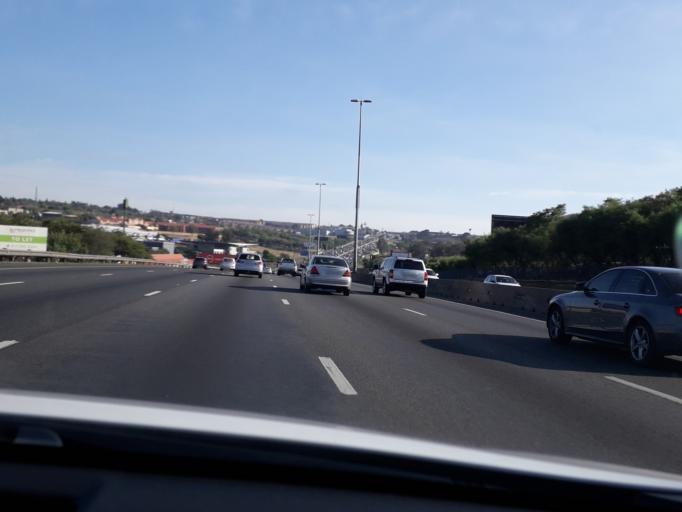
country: ZA
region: Gauteng
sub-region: City of Johannesburg Metropolitan Municipality
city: Midrand
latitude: -25.9998
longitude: 28.1211
